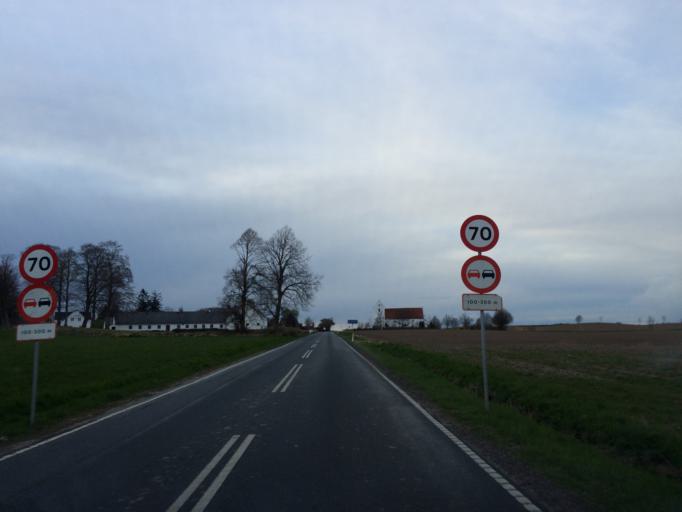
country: DK
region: South Denmark
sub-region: Odense Kommune
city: Bellinge
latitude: 55.3481
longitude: 10.2776
